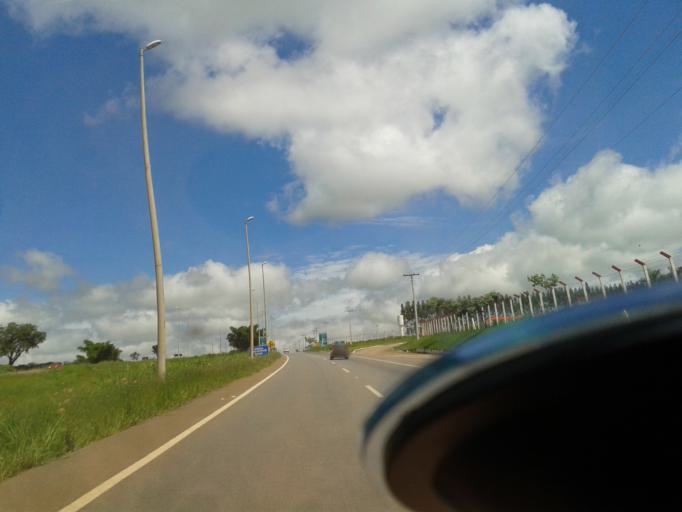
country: BR
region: Goias
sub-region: Goianira
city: Goianira
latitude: -16.4690
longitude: -49.4381
